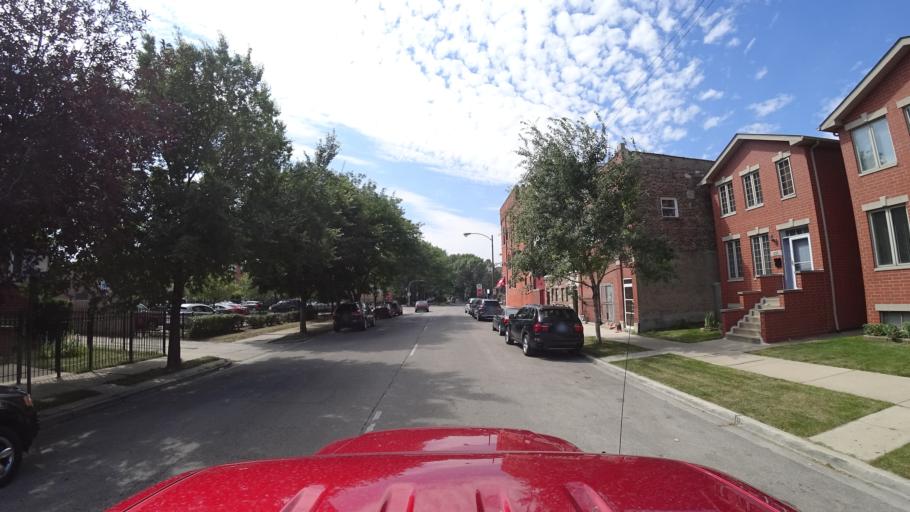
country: US
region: Illinois
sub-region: Cook County
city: Chicago
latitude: 41.8170
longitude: -87.6447
